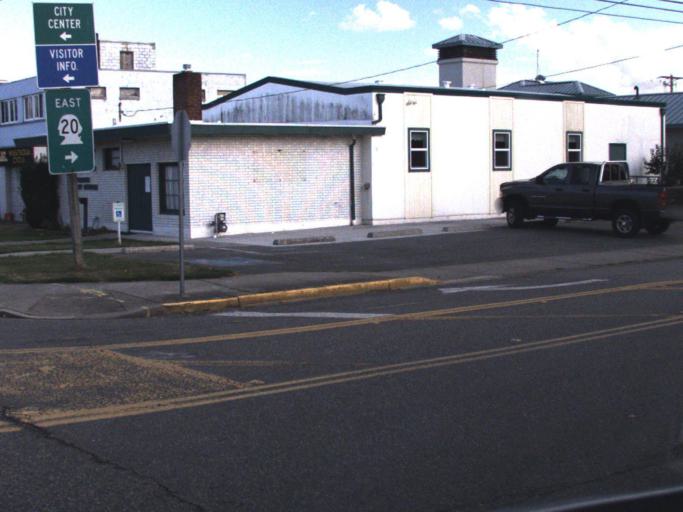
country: US
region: Washington
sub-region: Jefferson County
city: Port Hadlock-Irondale
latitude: 48.0195
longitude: -122.8305
